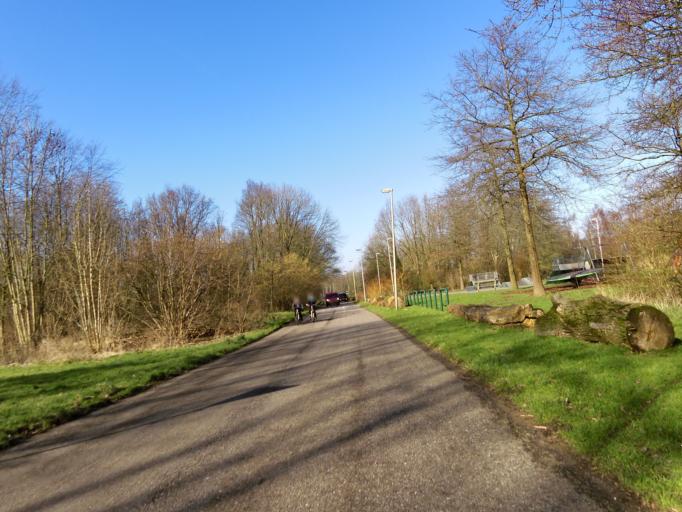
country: NL
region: South Holland
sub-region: Gemeente Leiderdorp
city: Leiderdorp
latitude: 52.1664
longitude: 4.5430
